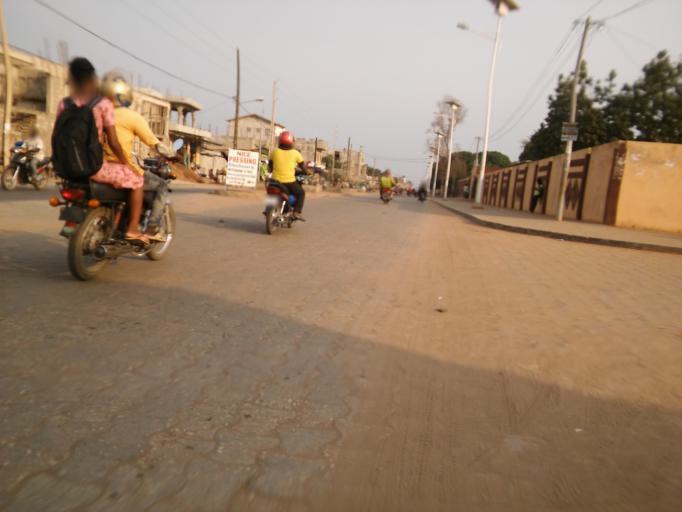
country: BJ
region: Atlantique
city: Abomey-Calavi
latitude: 6.4135
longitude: 2.3327
